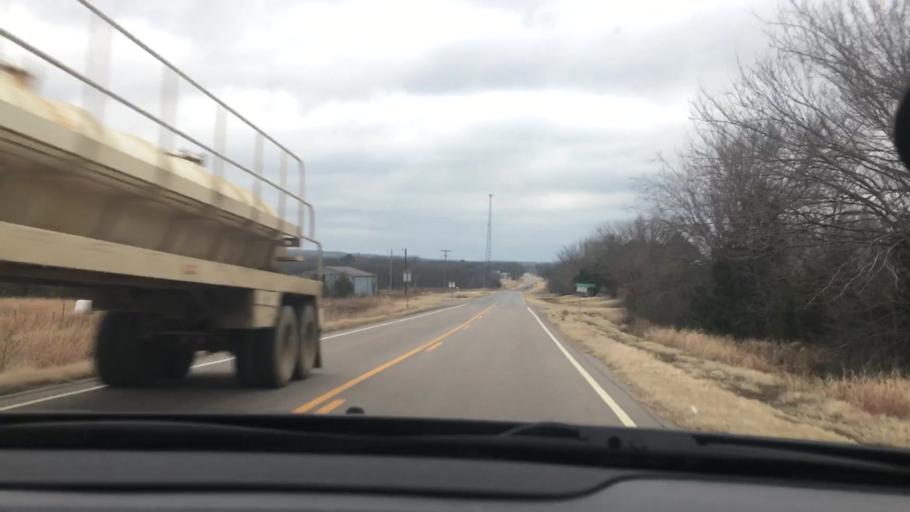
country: US
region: Oklahoma
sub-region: Coal County
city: Coalgate
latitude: 34.3749
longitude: -96.4059
